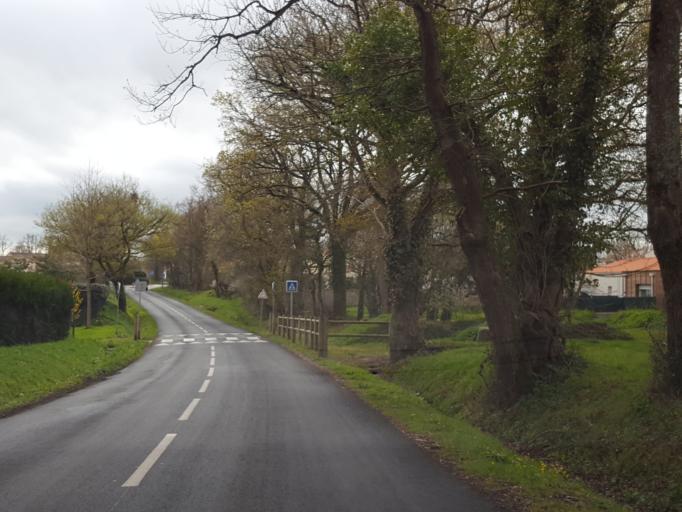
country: FR
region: Pays de la Loire
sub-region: Departement de la Vendee
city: La Roche-sur-Yon
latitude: 46.6699
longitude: -1.3979
